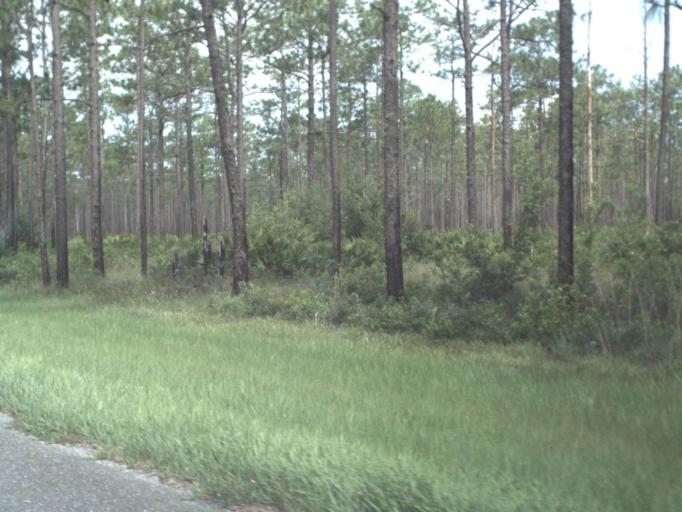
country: US
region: Florida
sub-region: Columbia County
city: Watertown
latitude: 30.1932
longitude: -82.5138
